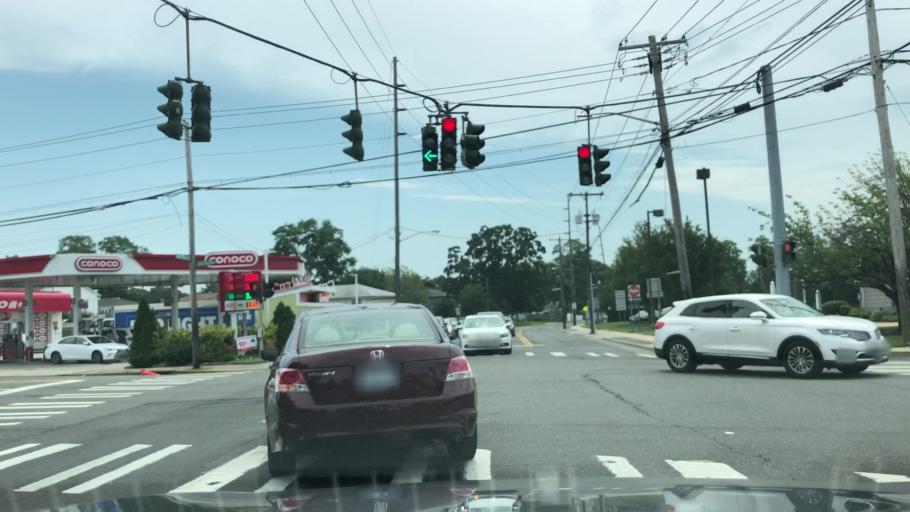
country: US
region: New York
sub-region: Nassau County
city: Massapequa
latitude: 40.6917
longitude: -73.4781
